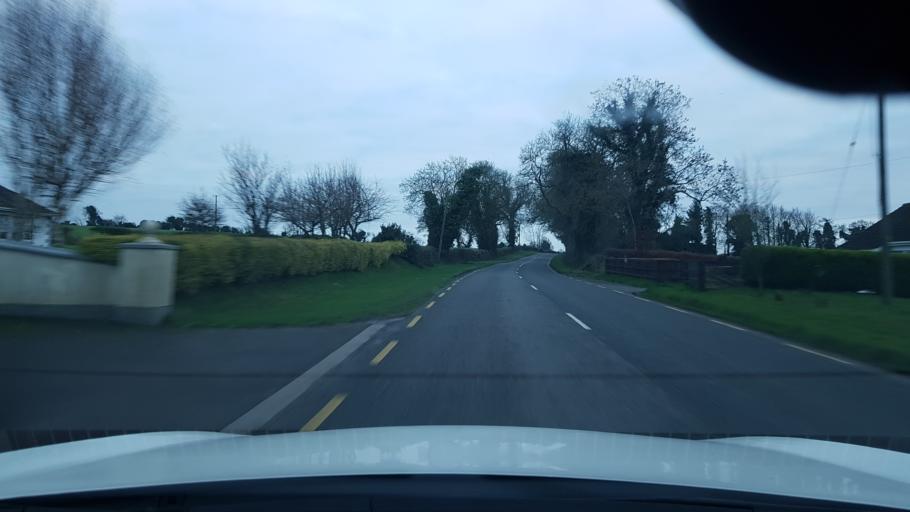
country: IE
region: Leinster
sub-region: An Mhi
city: Navan
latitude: 53.6897
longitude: -6.6736
